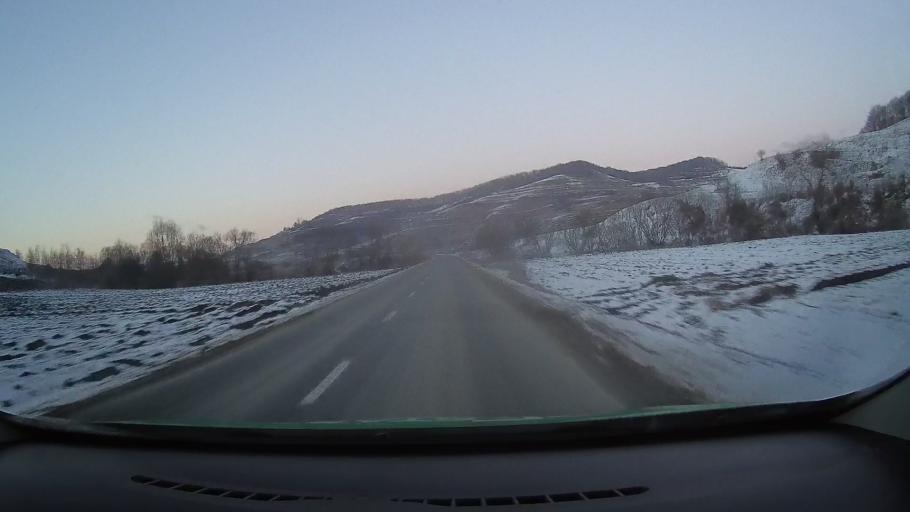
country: RO
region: Sibiu
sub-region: Comuna Atel
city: Atel
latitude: 46.1763
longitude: 24.4723
